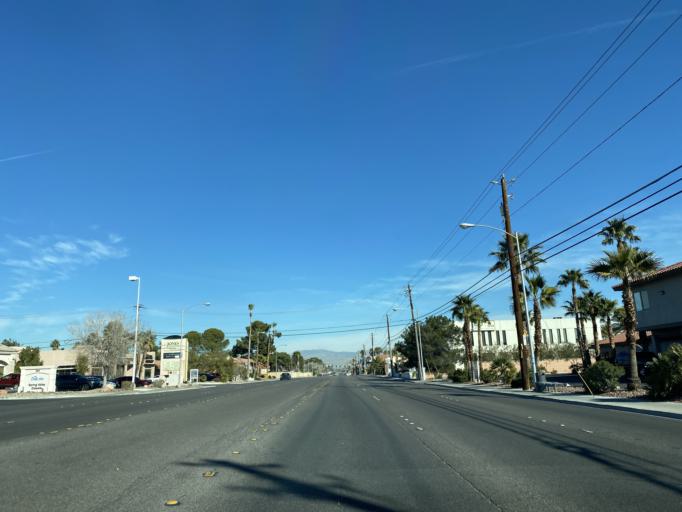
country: US
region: Nevada
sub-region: Clark County
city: Spring Valley
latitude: 36.1184
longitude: -115.2249
